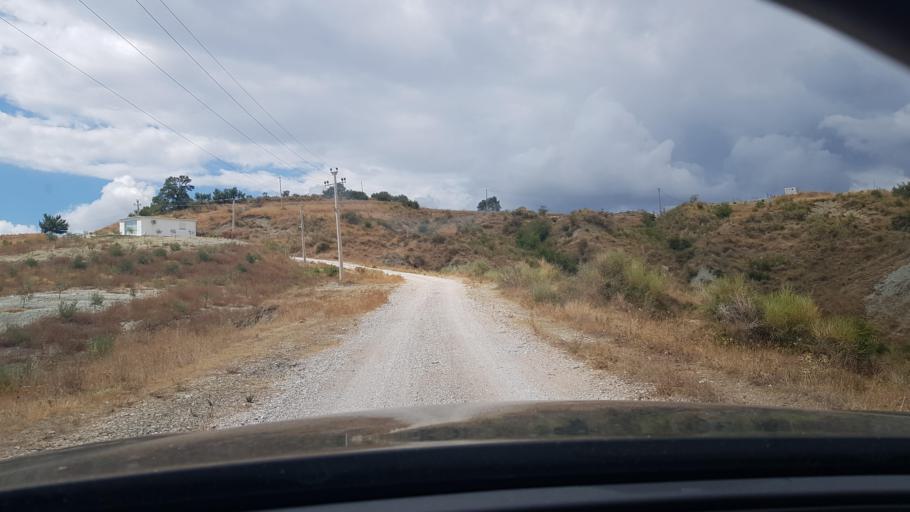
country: AL
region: Durres
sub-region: Rrethi i Durresit
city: Rrashbull
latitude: 41.2928
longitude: 19.5472
